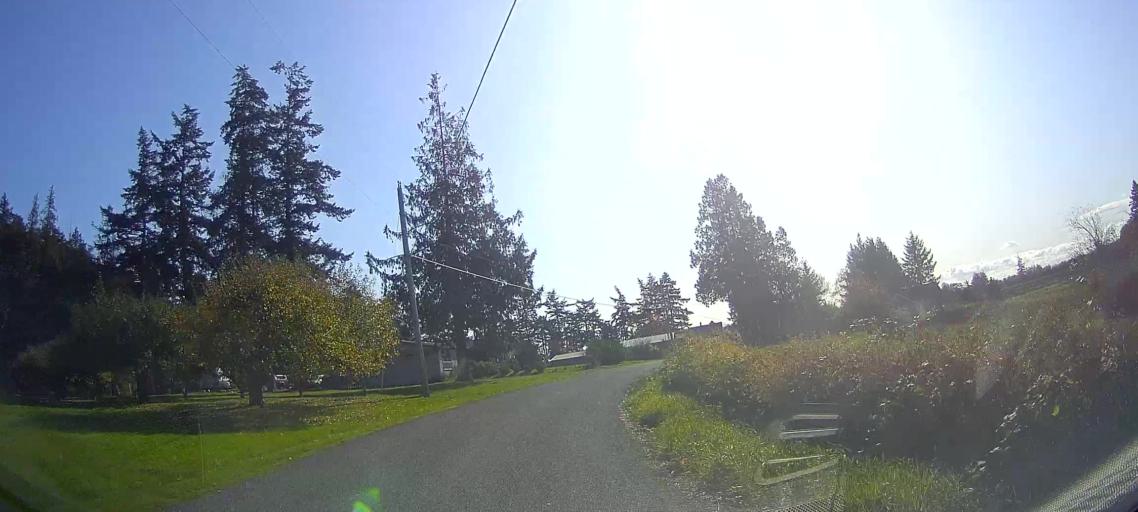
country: US
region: Washington
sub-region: Skagit County
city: Mount Vernon
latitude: 48.3654
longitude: -122.4419
